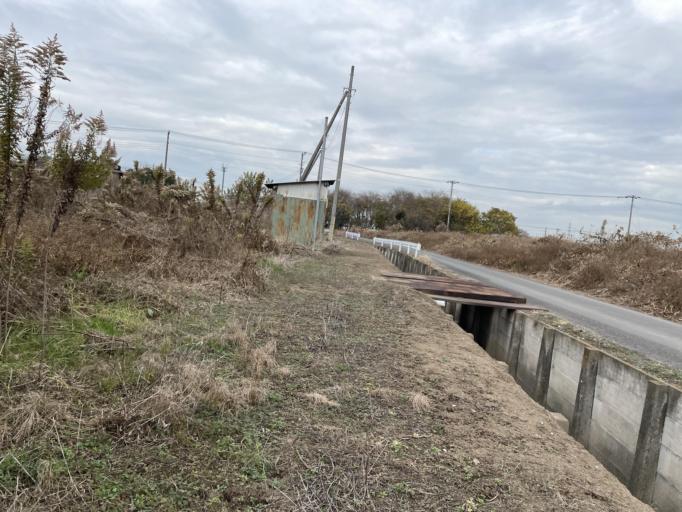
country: JP
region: Saitama
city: Shiraoka
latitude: 36.0287
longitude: 139.6448
